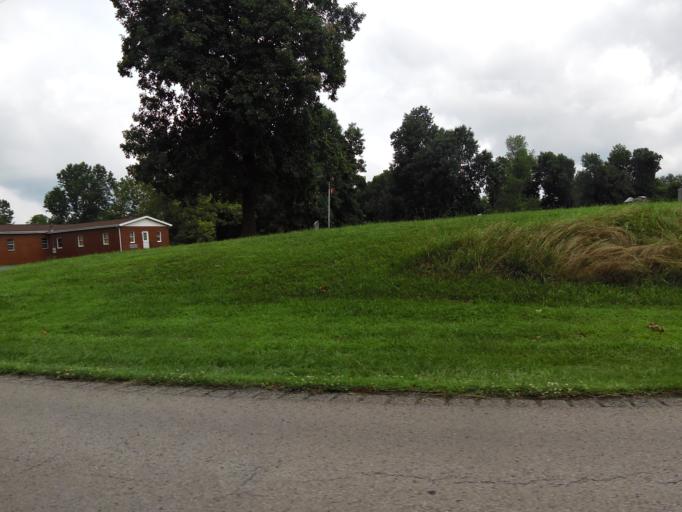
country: US
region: Kentucky
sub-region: Hopkins County
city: Madisonville
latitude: 37.3266
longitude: -87.3843
